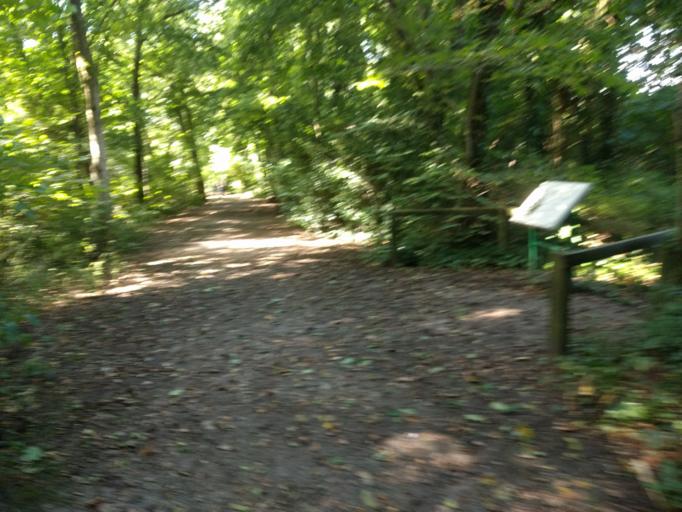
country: GB
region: England
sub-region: Warrington
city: Culcheth
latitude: 53.4252
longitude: -2.5039
